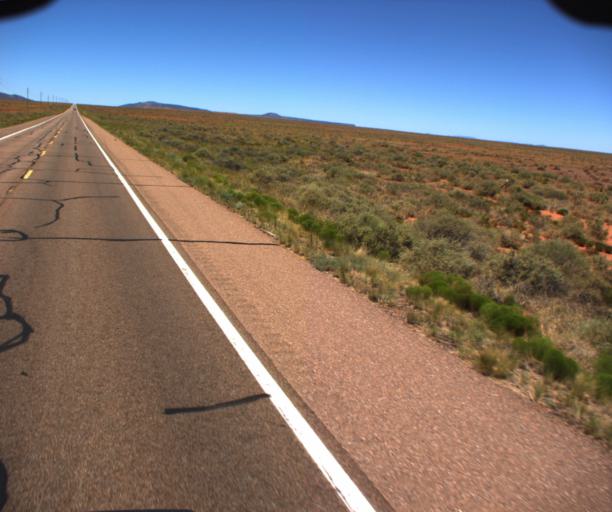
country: US
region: Arizona
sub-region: Coconino County
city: LeChee
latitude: 34.9556
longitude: -110.7532
